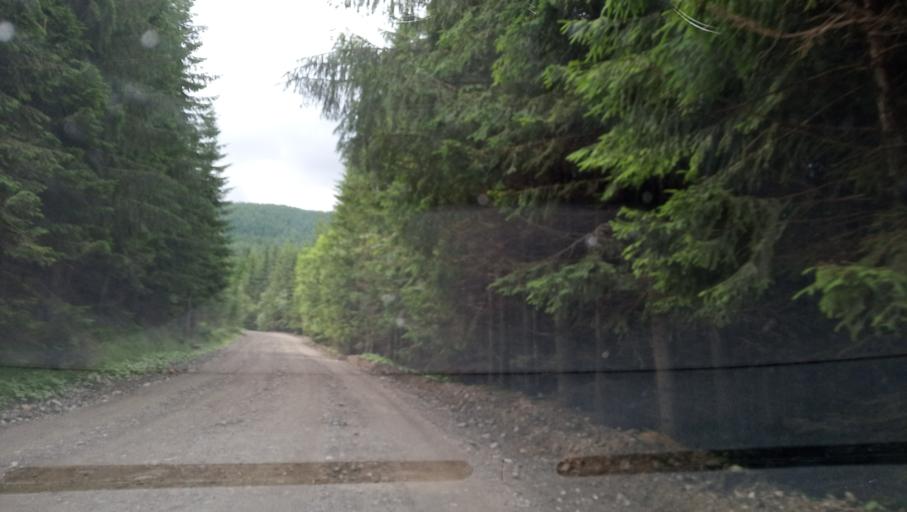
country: RO
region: Hunedoara
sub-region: Oras Petrila
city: Petrila
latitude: 45.4051
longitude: 23.5671
